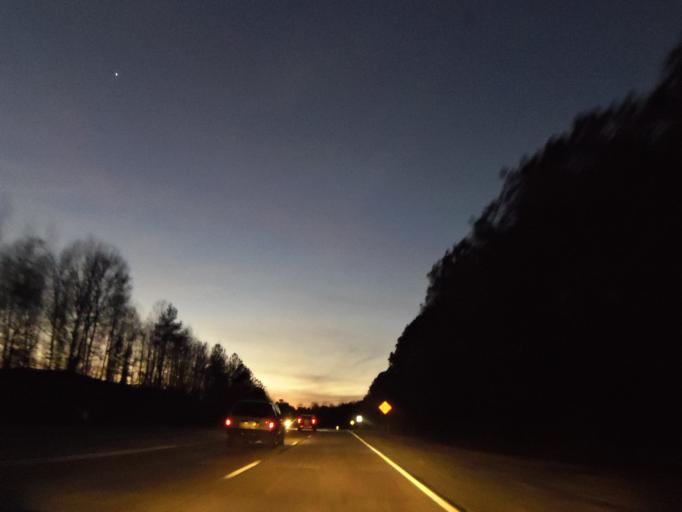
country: US
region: Georgia
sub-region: Whitfield County
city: Dalton
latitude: 34.8011
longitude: -84.9863
